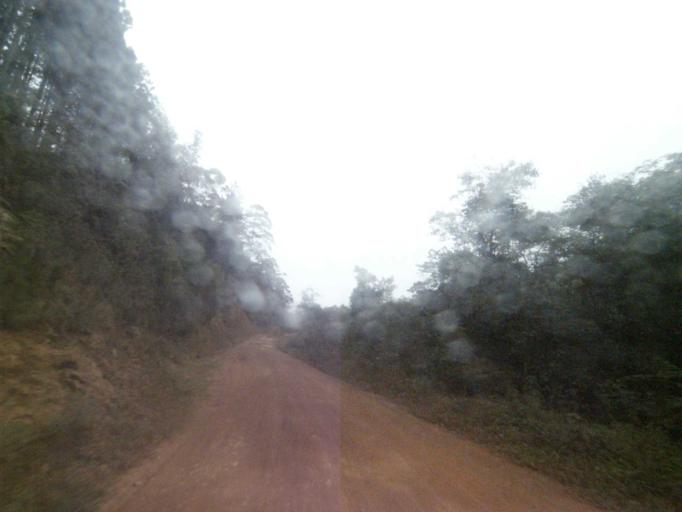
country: BR
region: Santa Catarina
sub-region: Anitapolis
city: Anitapolis
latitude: -27.8918
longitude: -49.1311
